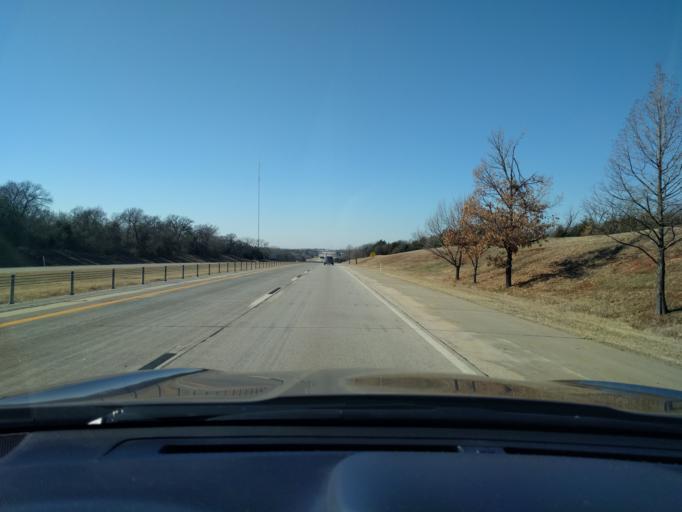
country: US
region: Oklahoma
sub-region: Oklahoma County
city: Edmond
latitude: 35.6014
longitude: -97.4607
